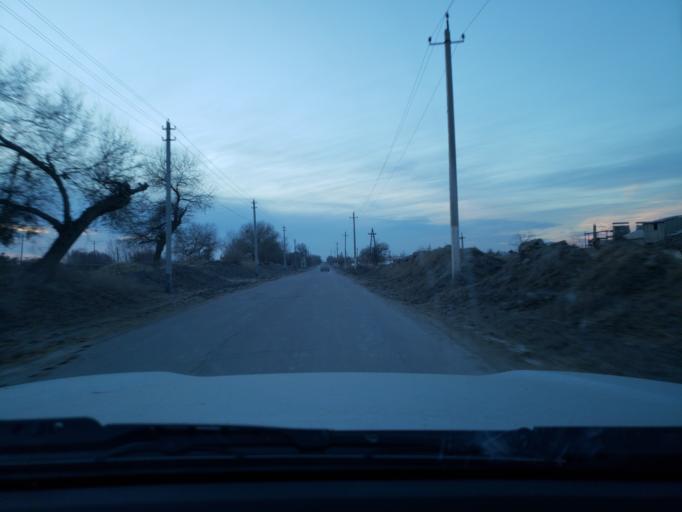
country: TM
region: Dasoguz
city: Tagta
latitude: 41.5836
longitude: 60.0655
